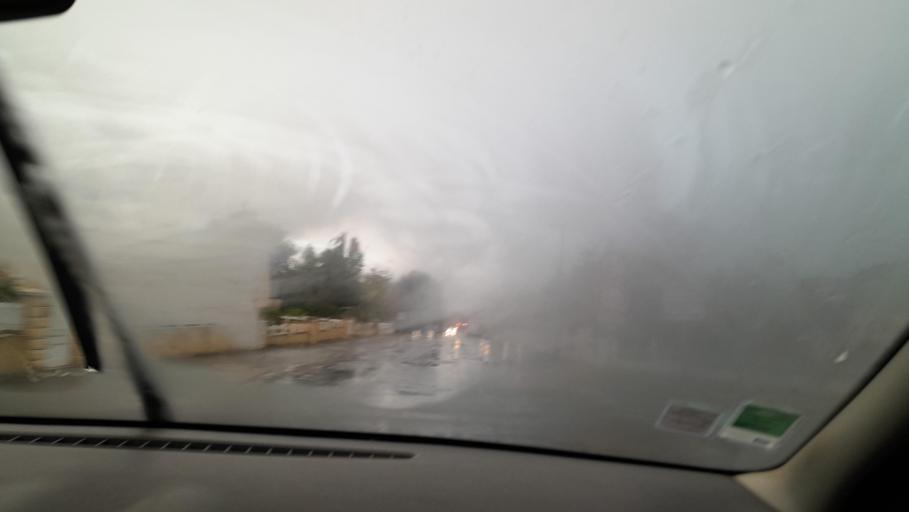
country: FR
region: Pays de la Loire
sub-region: Departement de la Mayenne
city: Ballots
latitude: 47.8918
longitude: -1.0468
